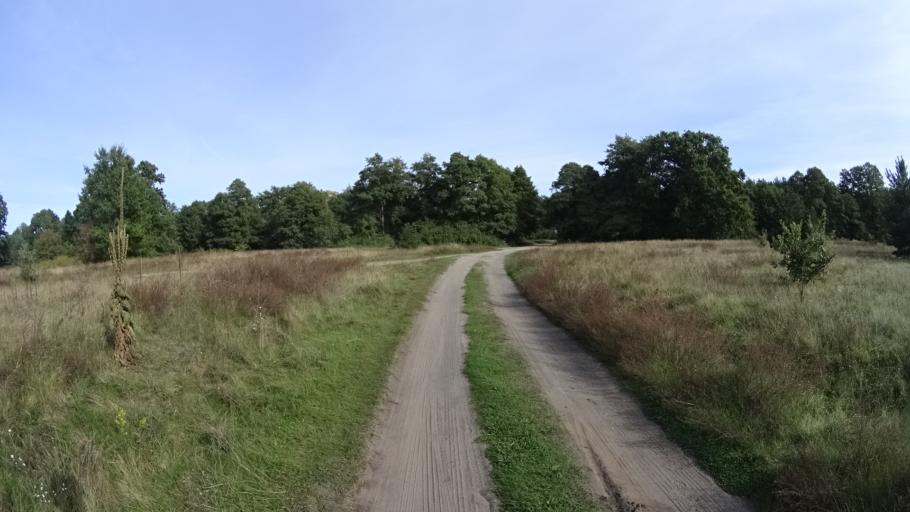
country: PL
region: Masovian Voivodeship
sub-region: Powiat legionowski
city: Serock
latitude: 52.5000
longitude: 21.0868
